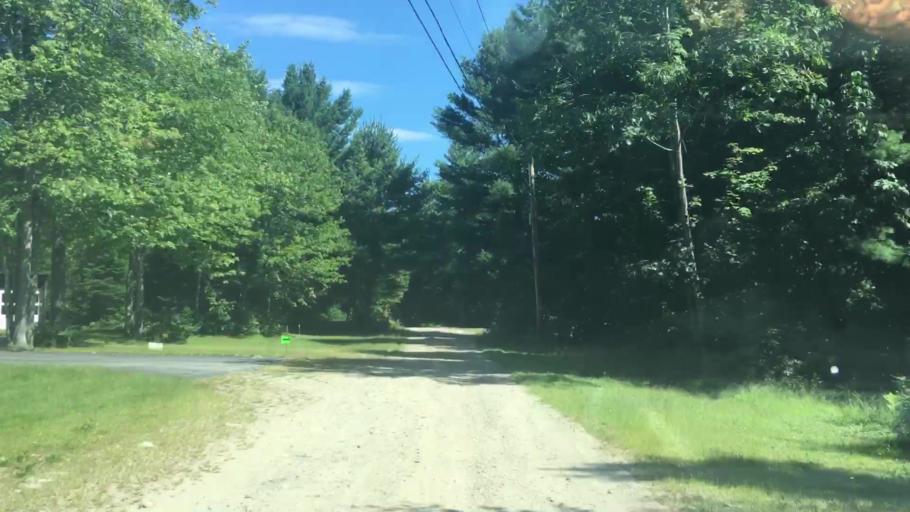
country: US
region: Maine
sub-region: Androscoggin County
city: Sabattus
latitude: 44.1220
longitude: -70.0299
